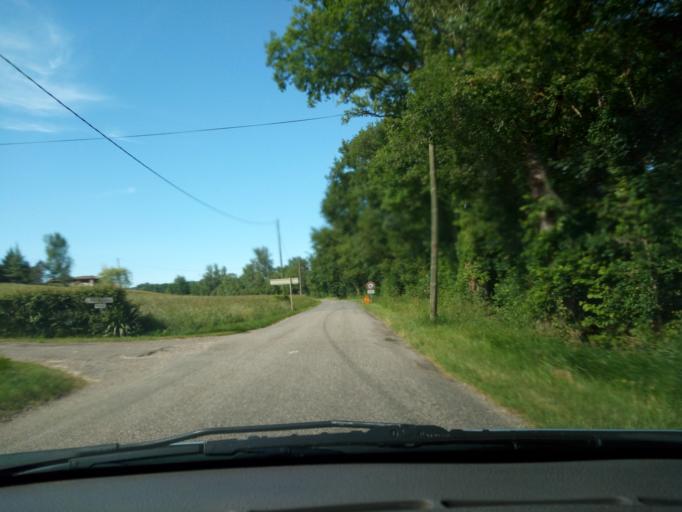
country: FR
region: Midi-Pyrenees
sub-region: Departement du Tarn-et-Garonne
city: Molieres
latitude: 44.2246
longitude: 1.3291
